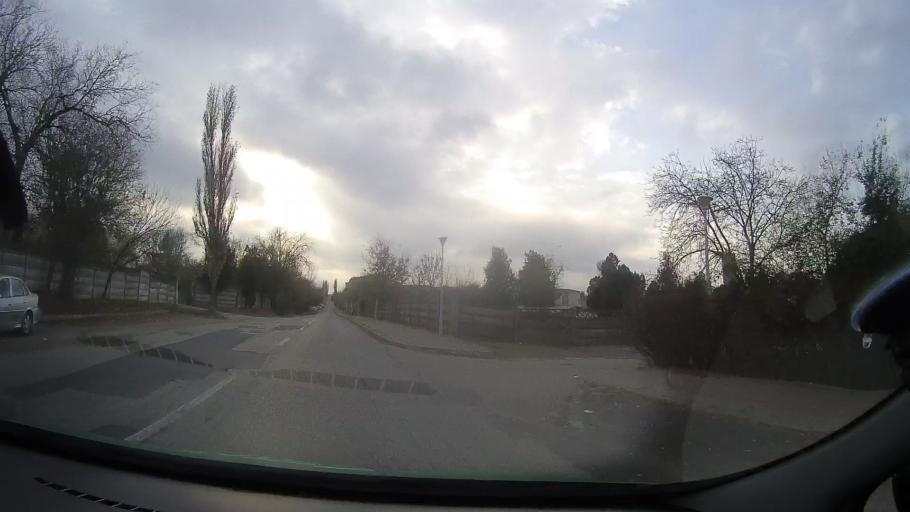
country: RO
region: Constanta
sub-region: Municipiul Medgidia
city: Medgidia
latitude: 44.2431
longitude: 28.2579
